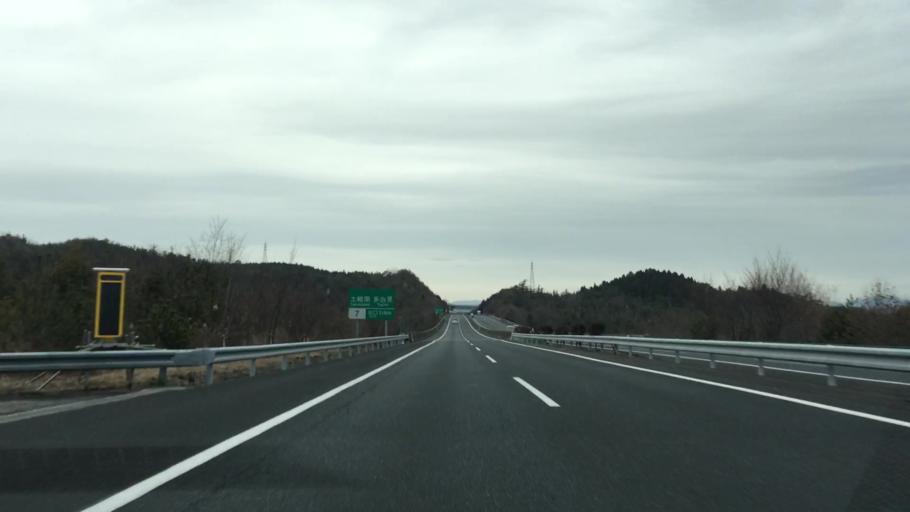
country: JP
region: Gifu
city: Toki
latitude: 35.3209
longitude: 137.1763
